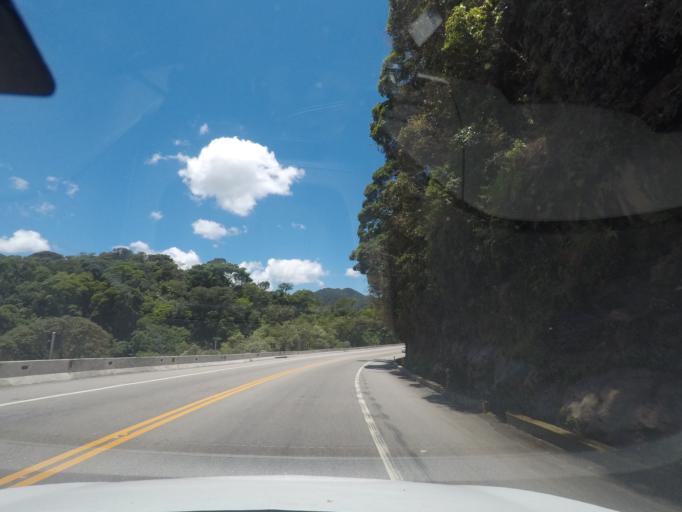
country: BR
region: Rio de Janeiro
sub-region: Teresopolis
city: Teresopolis
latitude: -22.4582
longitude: -42.9759
